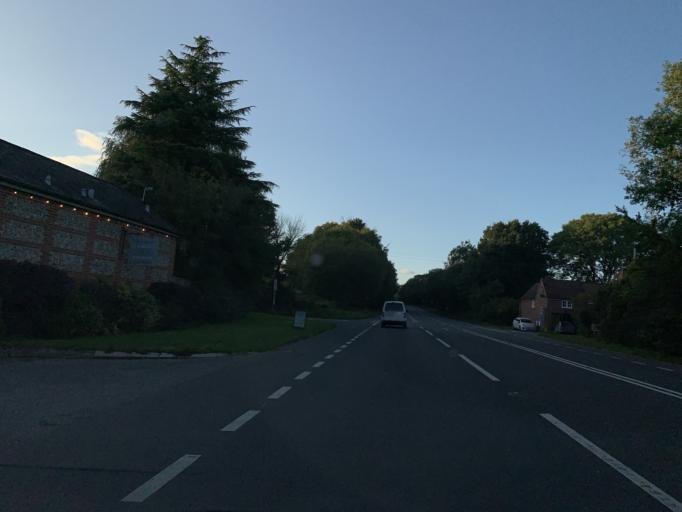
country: GB
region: England
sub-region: Wiltshire
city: Whiteparish
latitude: 51.0030
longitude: -1.6650
